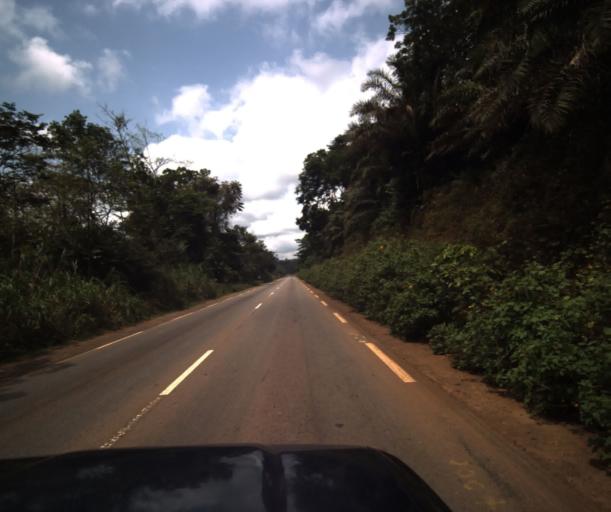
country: CM
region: Centre
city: Mbankomo
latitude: 3.7920
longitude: 11.3258
